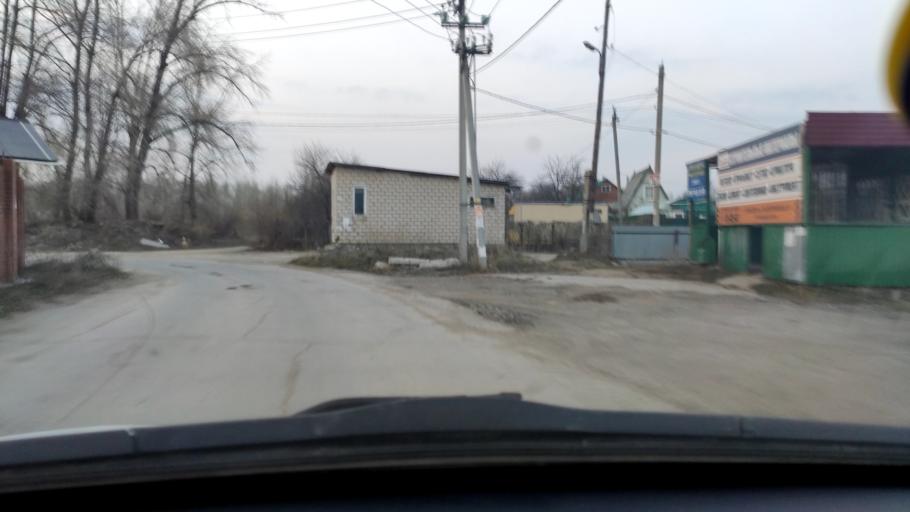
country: RU
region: Samara
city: Zhigulevsk
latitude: 53.4565
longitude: 49.5177
